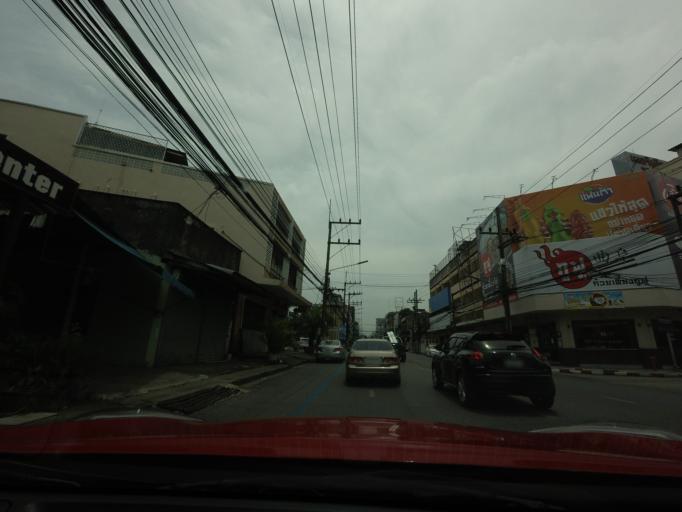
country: TH
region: Songkhla
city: Hat Yai
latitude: 6.9978
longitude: 100.4749
